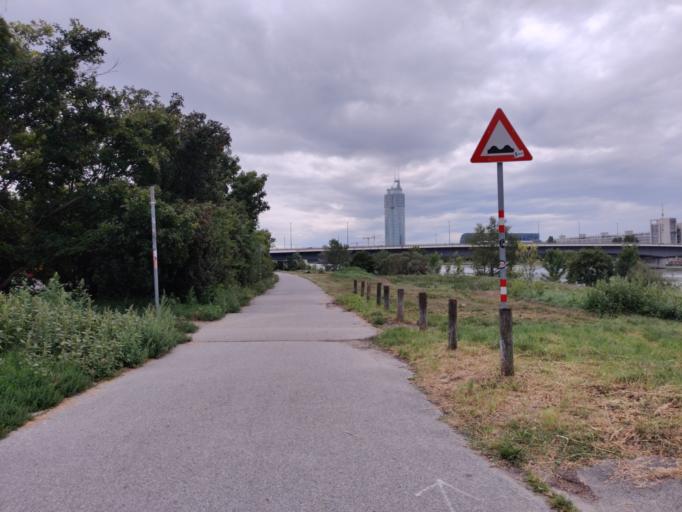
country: AT
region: Vienna
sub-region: Wien Stadt
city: Vienna
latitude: 48.2498
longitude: 16.3847
